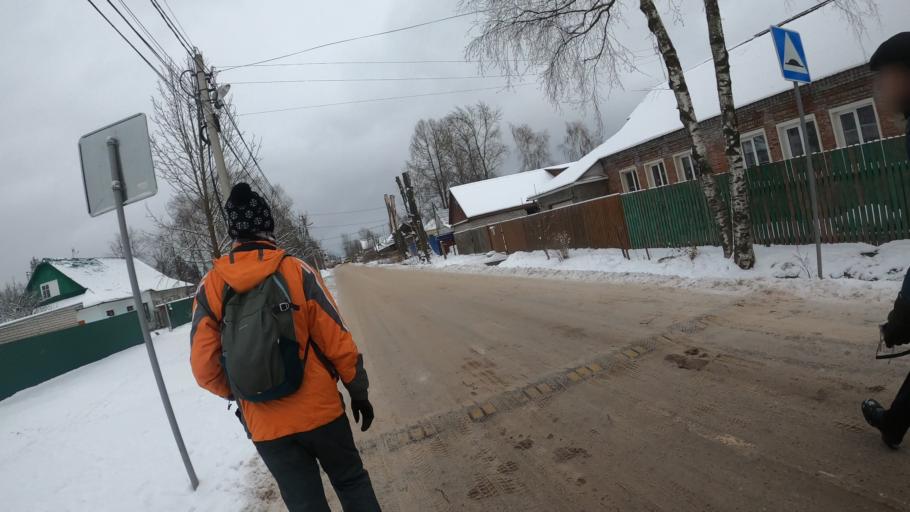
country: RU
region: Jaroslavl
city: Pereslavl'-Zalesskiy
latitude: 56.7288
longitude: 38.8374
